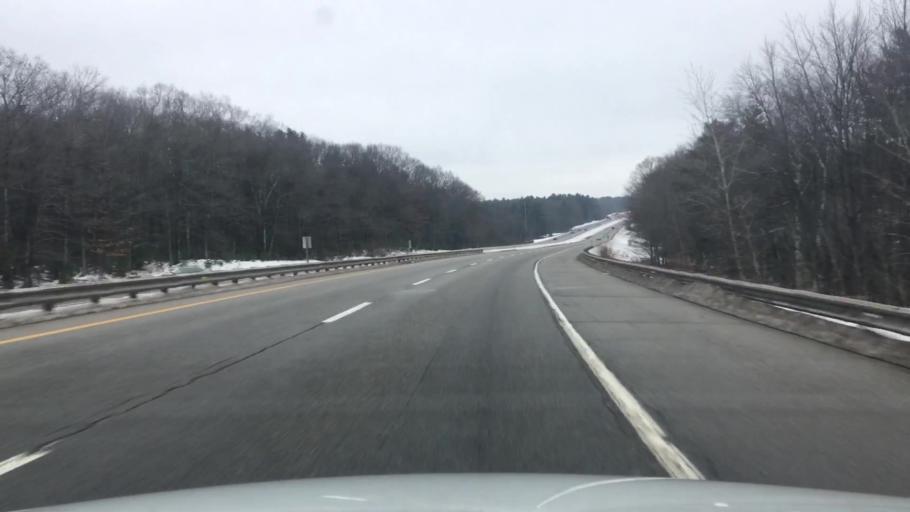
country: US
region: Maine
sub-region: Cumberland County
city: Scarborough
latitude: 43.6058
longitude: -70.3191
